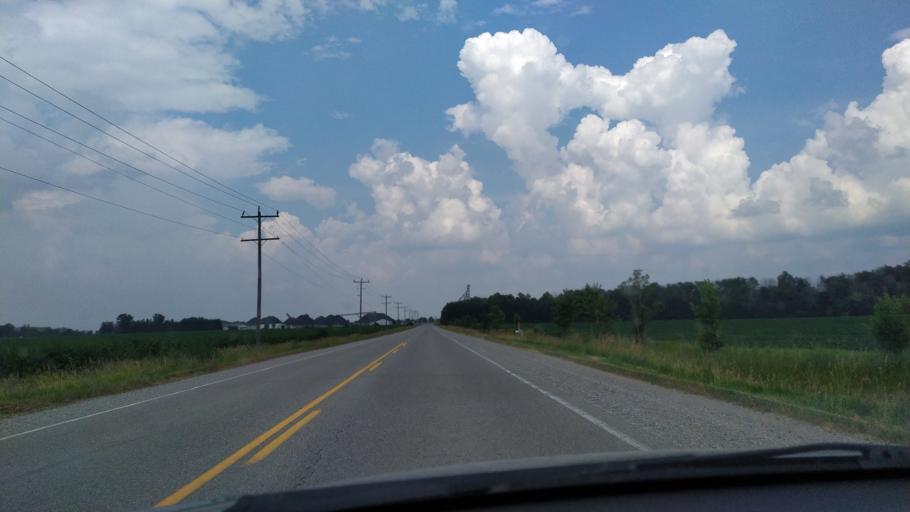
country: CA
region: Ontario
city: Dorchester
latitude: 43.1635
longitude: -81.1483
